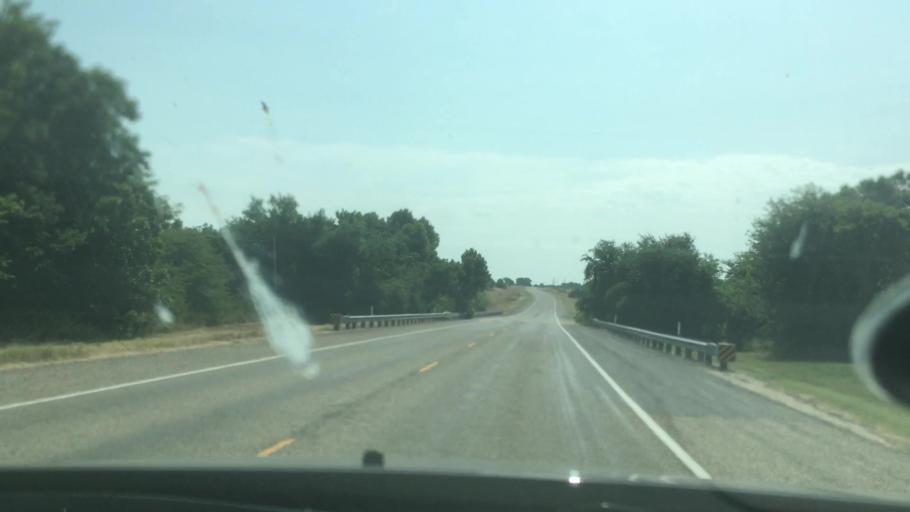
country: US
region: Texas
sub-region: Grayson County
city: Pottsboro
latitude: 33.8021
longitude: -96.6670
